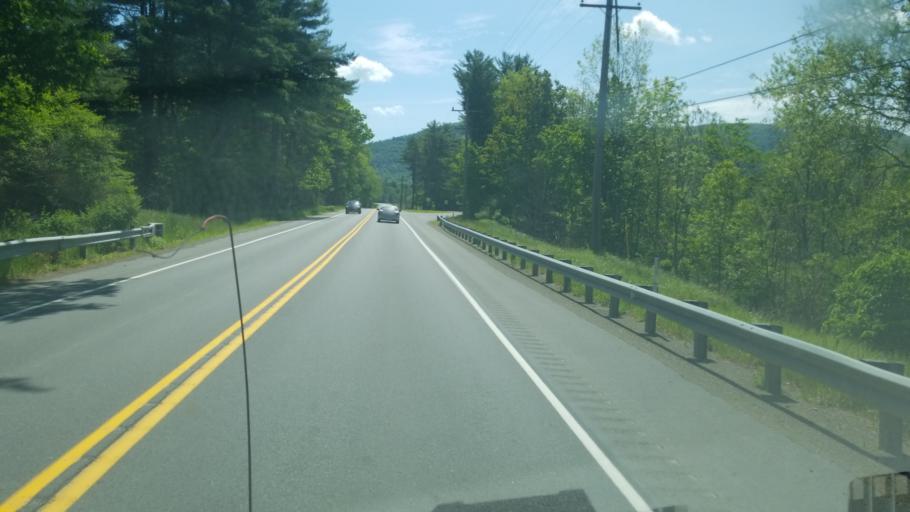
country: US
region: Pennsylvania
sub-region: Potter County
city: Galeton
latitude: 41.7491
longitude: -77.5494
